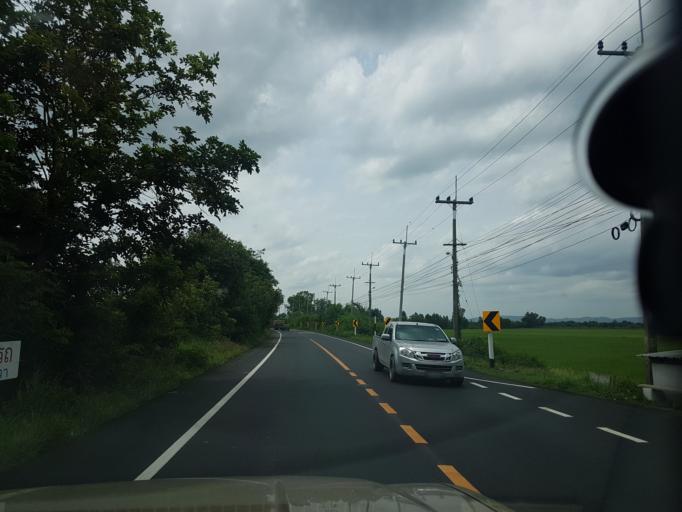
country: TH
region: Sara Buri
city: Nong Khae
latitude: 14.2966
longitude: 100.8917
